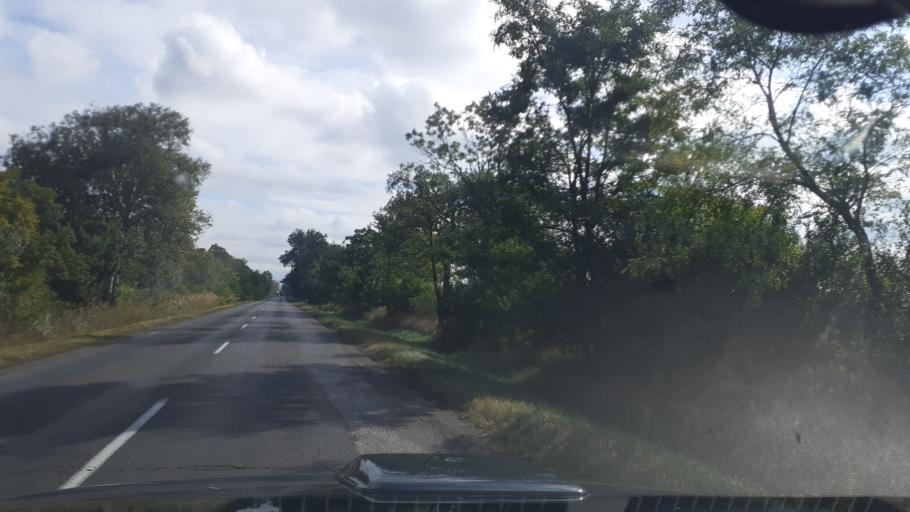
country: HU
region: Bacs-Kiskun
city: Solt
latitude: 46.7986
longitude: 19.1162
